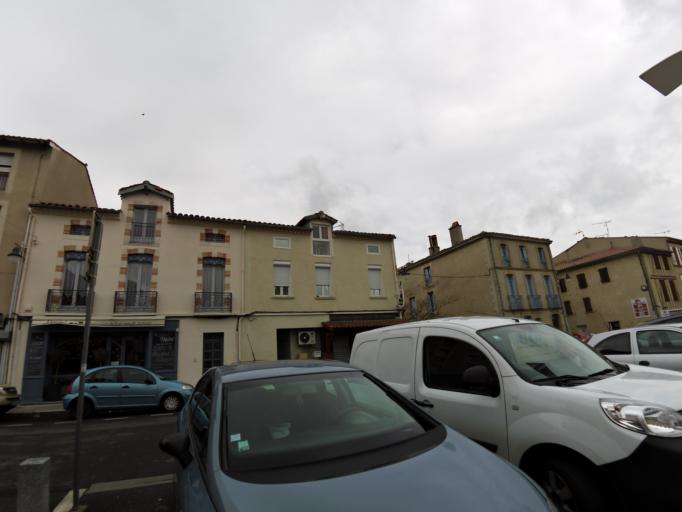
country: FR
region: Midi-Pyrenees
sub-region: Departement de la Haute-Garonne
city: Revel
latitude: 43.4569
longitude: 2.0029
